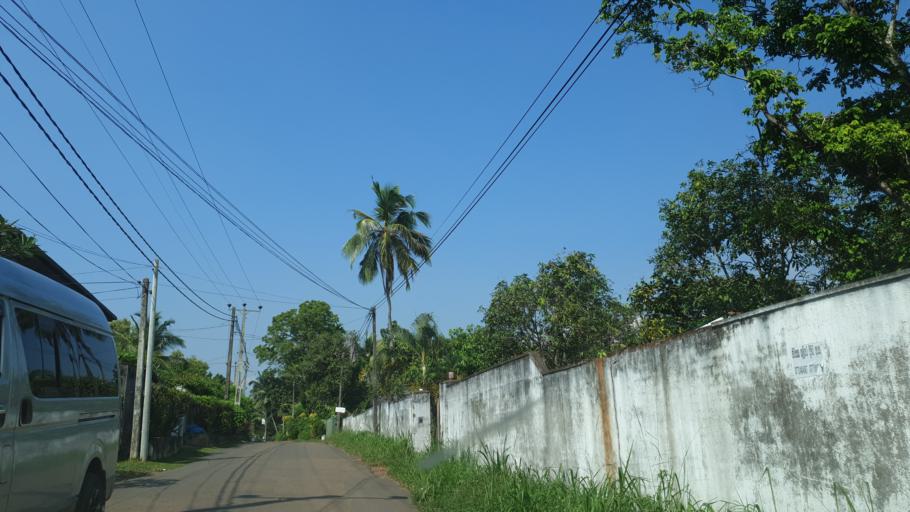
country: LK
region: Western
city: Moratuwa
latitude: 6.7612
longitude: 79.9244
